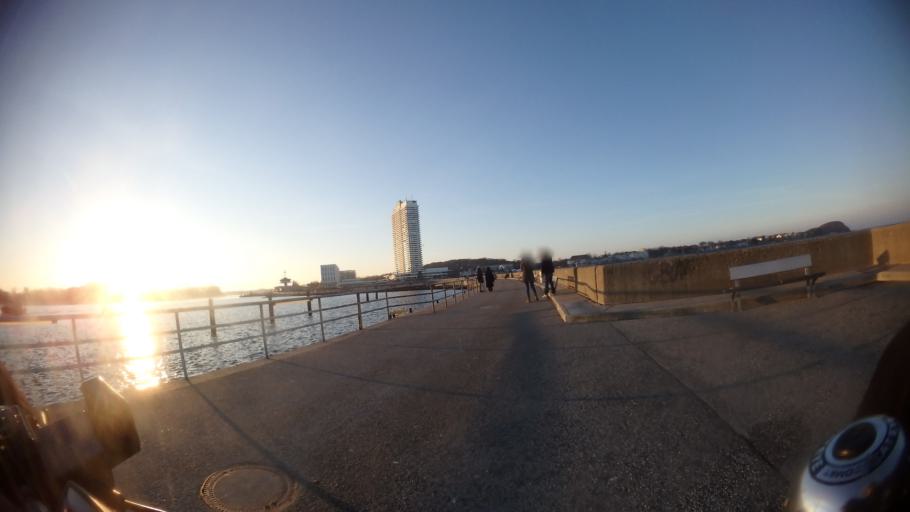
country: DE
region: Schleswig-Holstein
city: Travemuende
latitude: 53.9620
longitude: 10.8885
